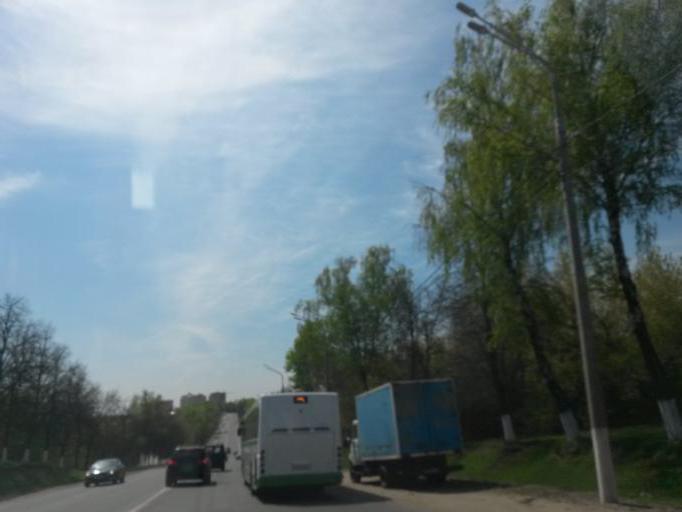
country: RU
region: Moskovskaya
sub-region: Podol'skiy Rayon
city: Podol'sk
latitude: 55.4592
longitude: 37.5584
